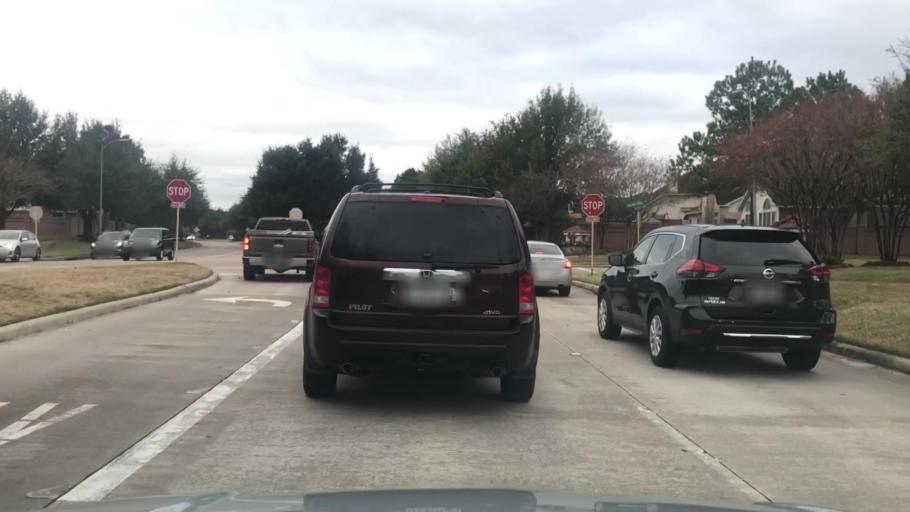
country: US
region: Texas
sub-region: Fort Bend County
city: Cinco Ranch
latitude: 29.7494
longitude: -95.7868
